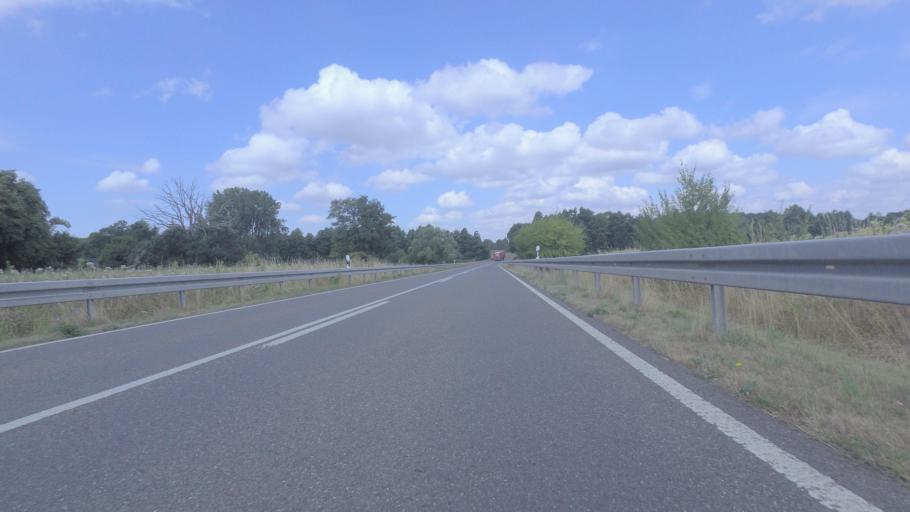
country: DE
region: Brandenburg
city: Walsleben
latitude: 52.9955
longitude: 12.6501
